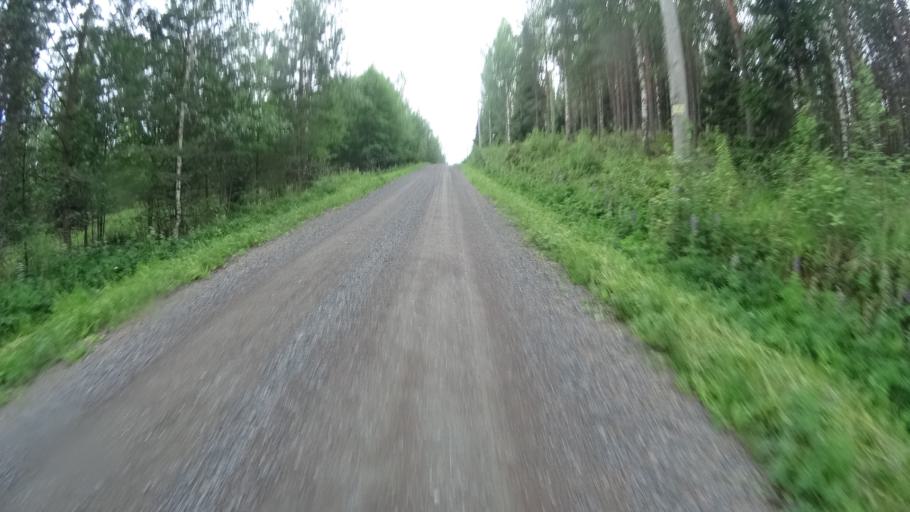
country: FI
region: Uusimaa
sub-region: Helsinki
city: Karkkila
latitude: 60.5885
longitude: 24.1629
